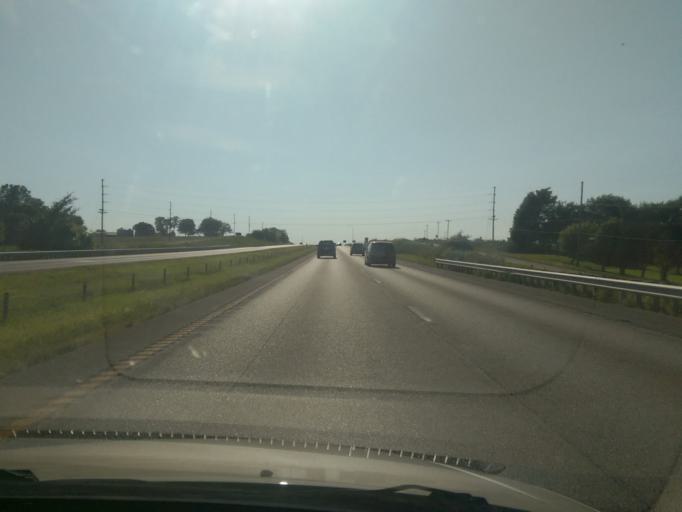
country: US
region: Missouri
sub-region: Lafayette County
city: Odessa
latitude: 39.0039
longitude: -93.8396
